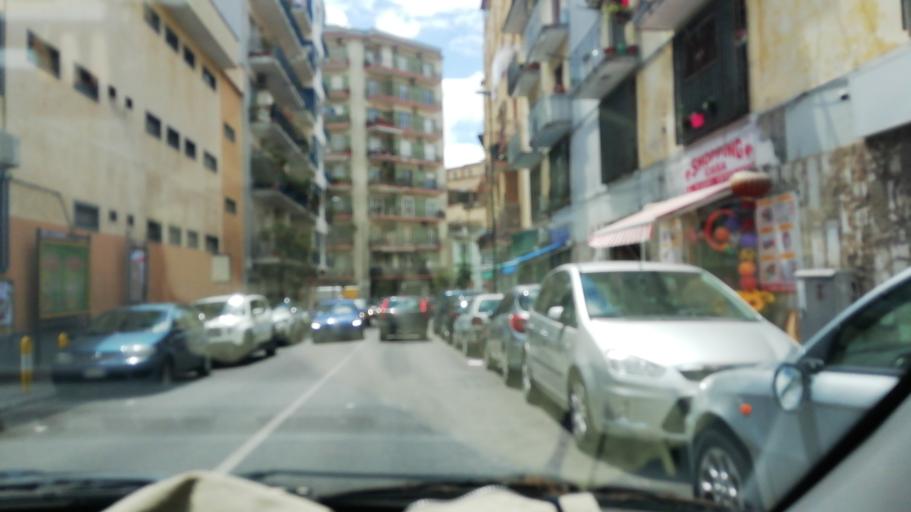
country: IT
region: Campania
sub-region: Provincia di Napoli
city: Napoli
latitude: 40.8499
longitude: 14.2203
